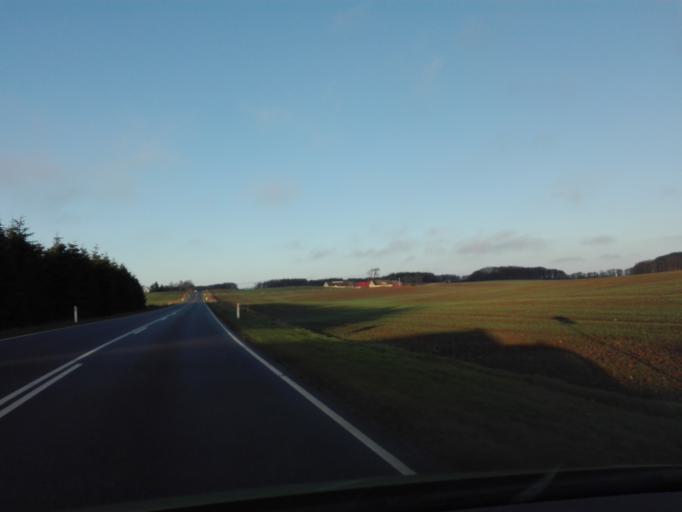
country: DK
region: Central Jutland
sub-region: Skanderborg Kommune
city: Skanderborg
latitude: 56.0709
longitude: 9.8954
